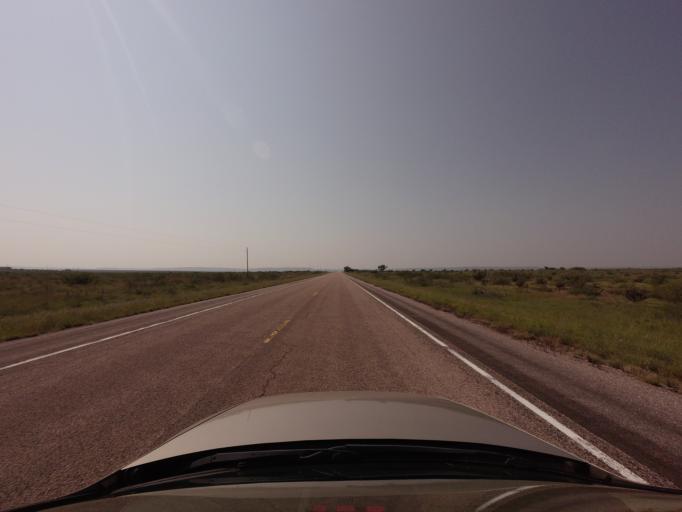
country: US
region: New Mexico
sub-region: Quay County
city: Tucumcari
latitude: 34.9302
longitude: -103.7602
